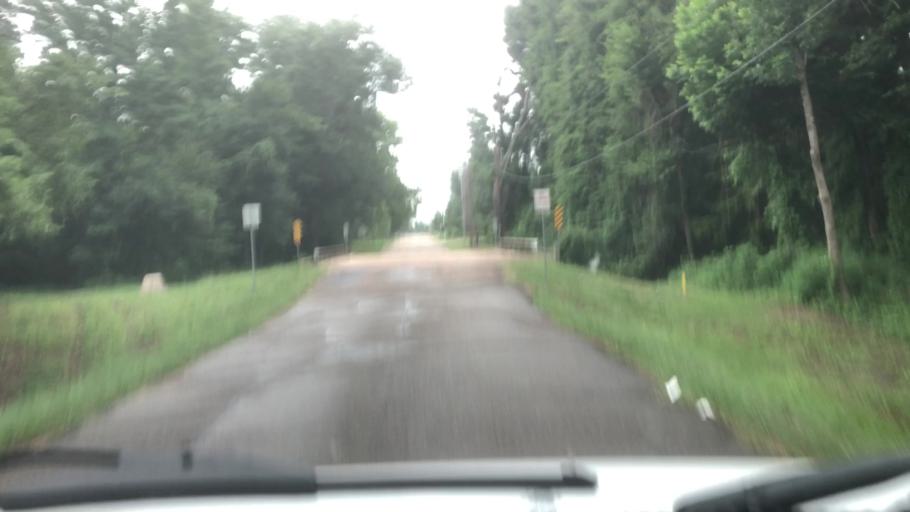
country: US
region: Texas
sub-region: Bowie County
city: Wake Village
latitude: 33.3978
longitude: -94.0835
